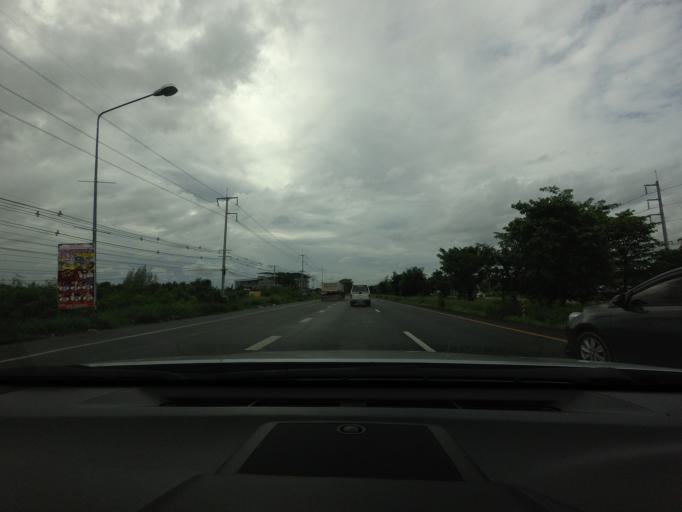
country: TH
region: Prachuap Khiri Khan
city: Hua Hin
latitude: 12.5797
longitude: 99.8661
